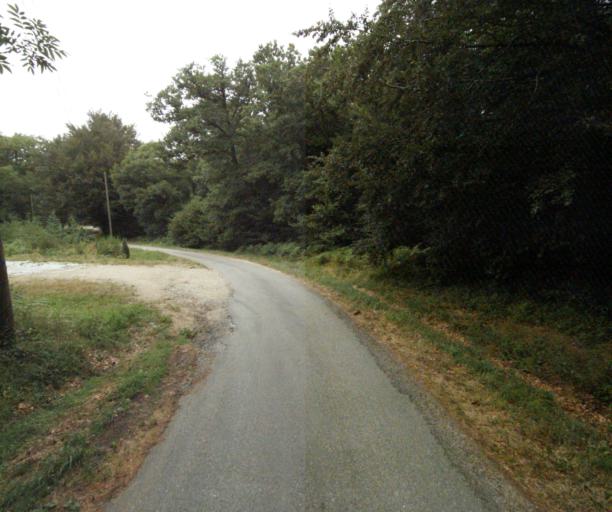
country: FR
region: Midi-Pyrenees
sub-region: Departement du Tarn
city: Soreze
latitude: 43.4205
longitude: 2.0470
